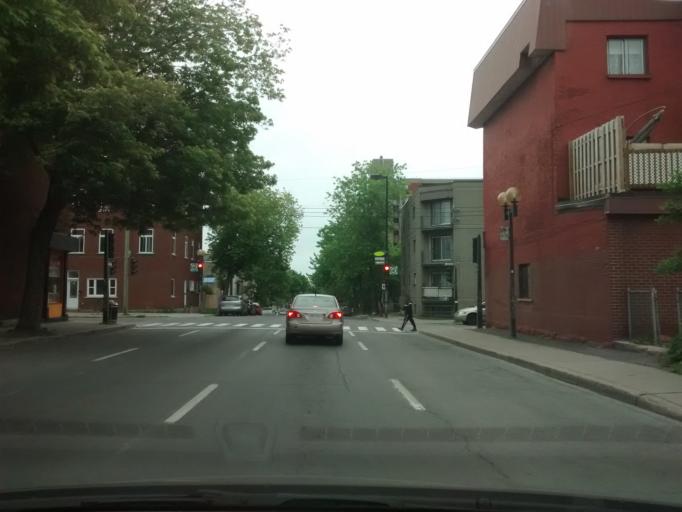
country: CA
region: Quebec
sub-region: Monteregie
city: Longueuil
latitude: 45.5309
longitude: -73.5495
